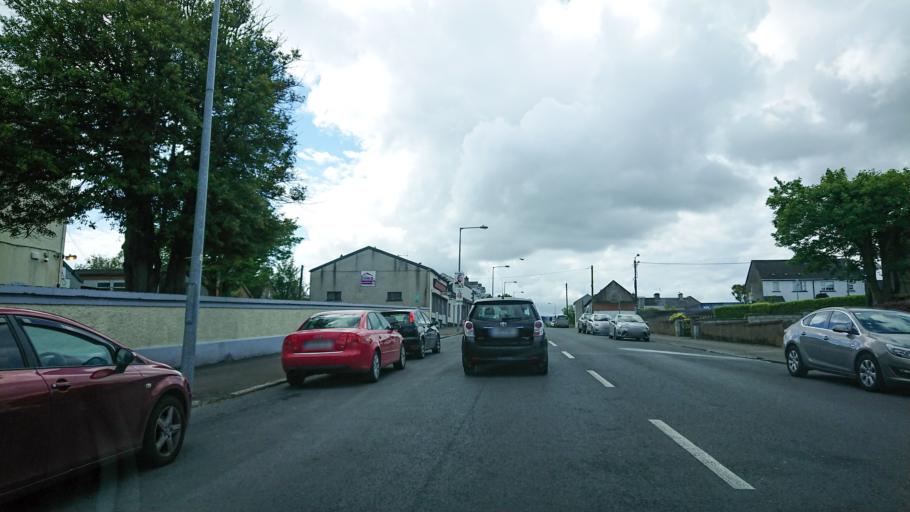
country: IE
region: Munster
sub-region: Waterford
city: Dungarvan
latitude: 52.0903
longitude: -7.6293
